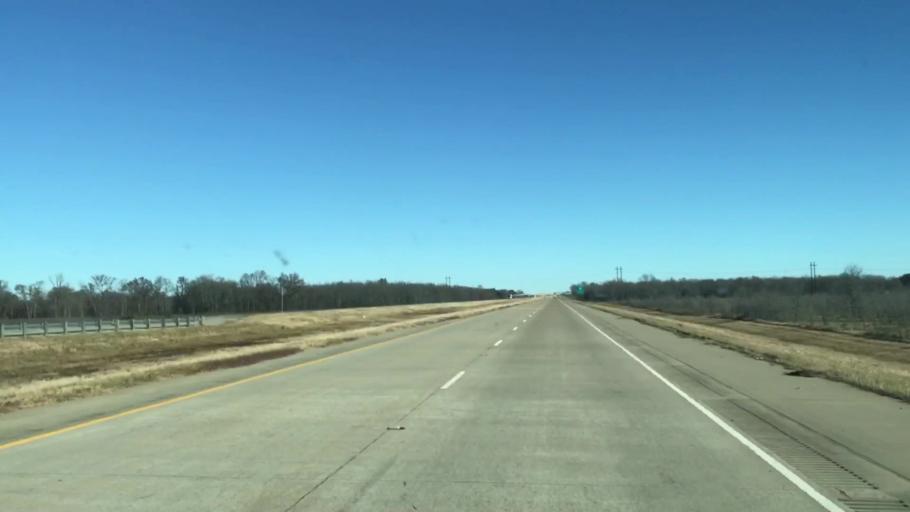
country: US
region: Louisiana
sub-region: Caddo Parish
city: Vivian
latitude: 32.8299
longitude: -93.8752
